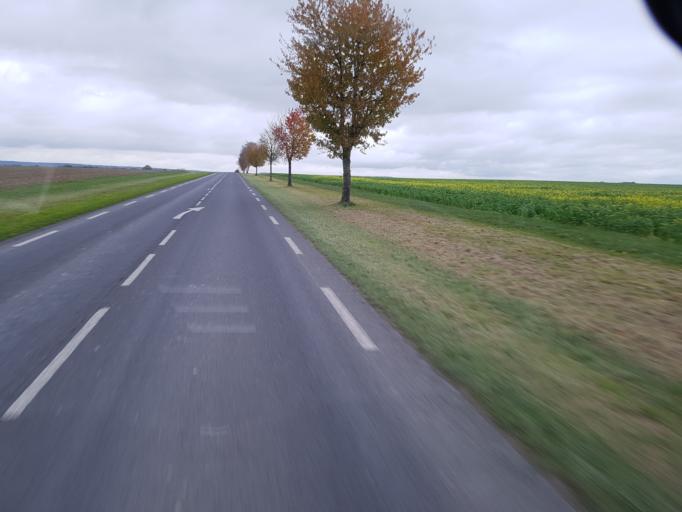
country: FR
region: Champagne-Ardenne
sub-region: Departement de la Marne
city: Saint-Just-Sauvage
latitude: 48.6259
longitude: 3.7849
